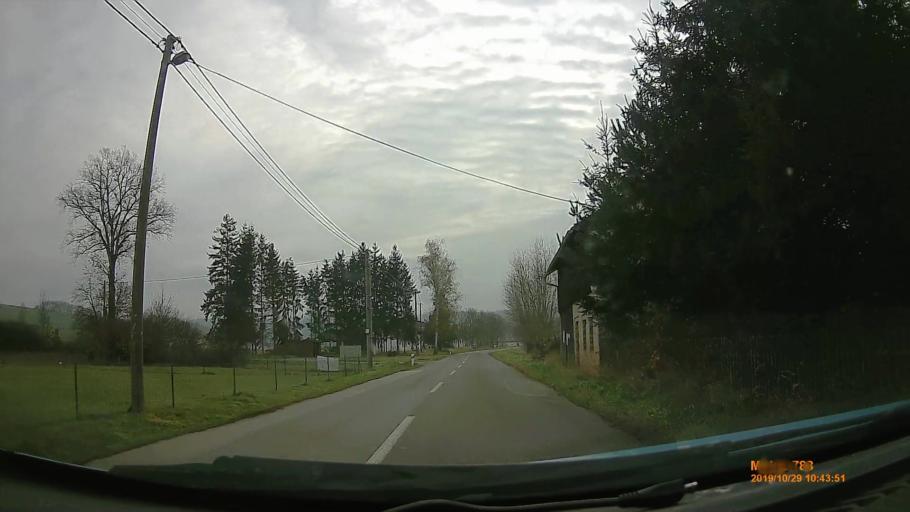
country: PL
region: Lower Silesian Voivodeship
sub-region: Powiat klodzki
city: Radkow
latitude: 50.5541
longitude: 16.3959
